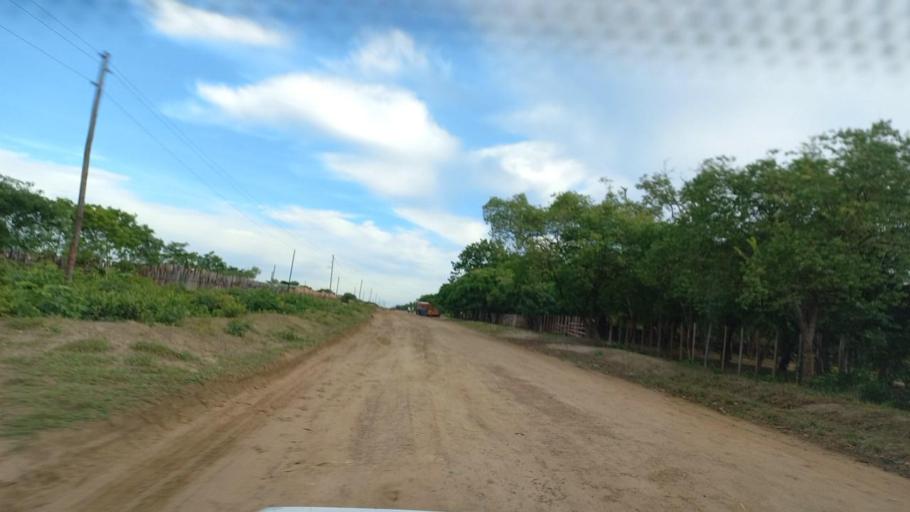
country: ZM
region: North-Western
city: Kabompo
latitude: -13.4207
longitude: 24.3223
